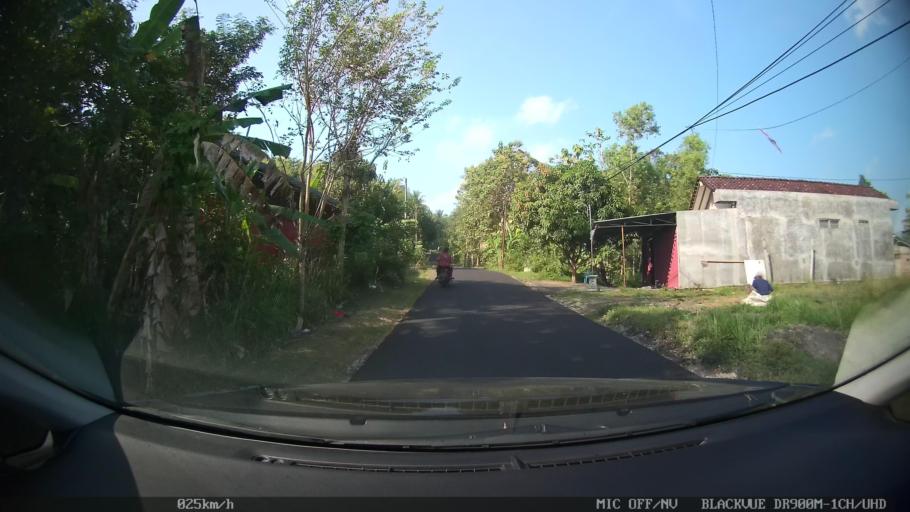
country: ID
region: Daerah Istimewa Yogyakarta
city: Kasihan
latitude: -7.8264
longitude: 110.2734
